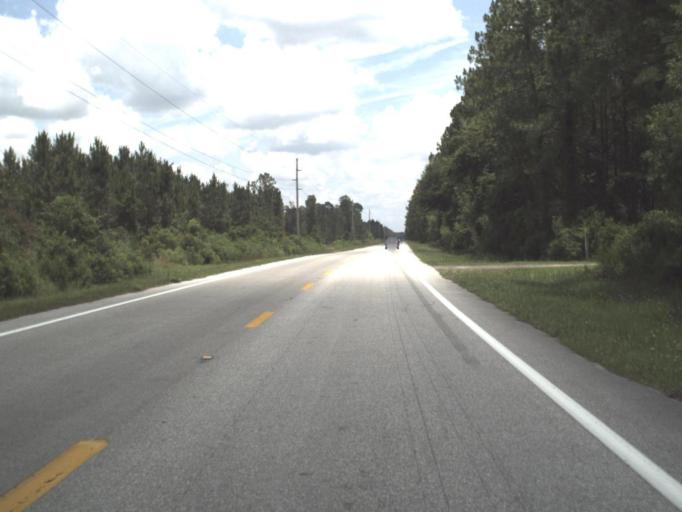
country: US
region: Florida
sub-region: Levy County
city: Bronson
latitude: 29.4228
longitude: -82.6730
